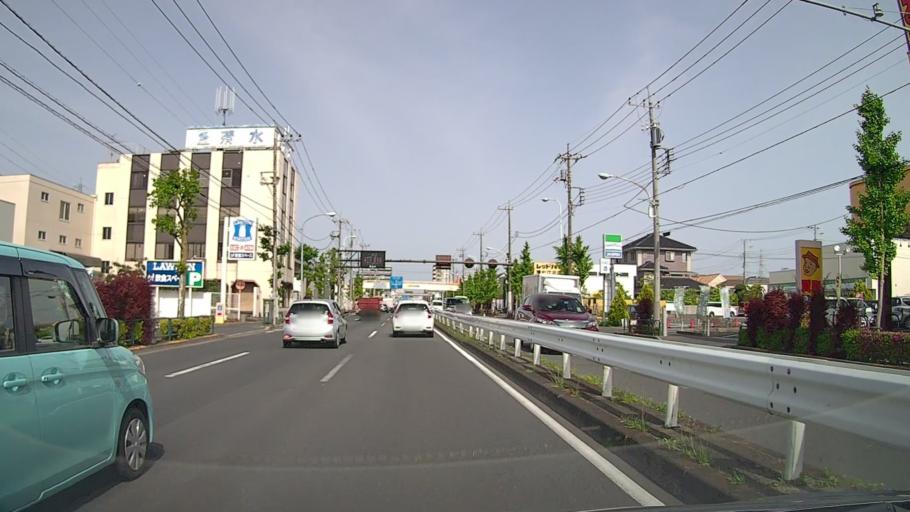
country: JP
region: Saitama
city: Kawaguchi
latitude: 35.7783
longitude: 139.7621
